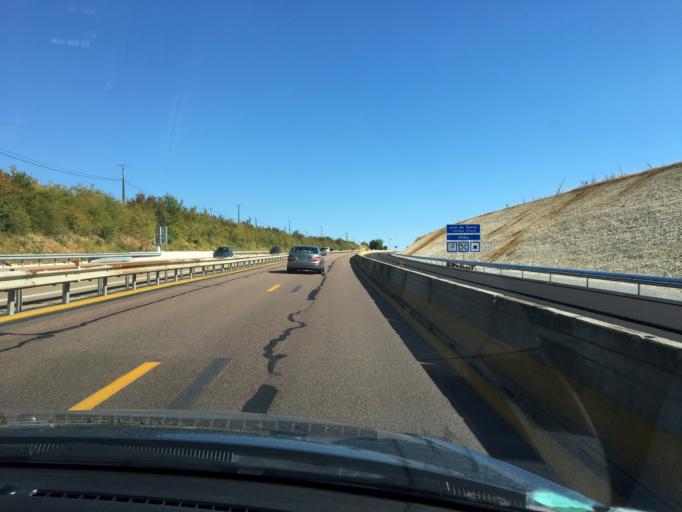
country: FR
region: Bourgogne
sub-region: Departement de l'Yonne
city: Venoy
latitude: 47.7945
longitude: 3.6641
